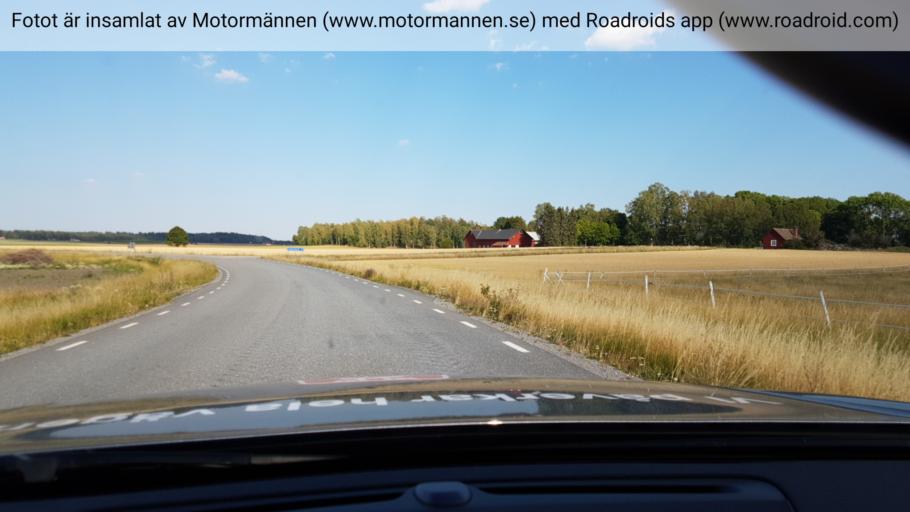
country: SE
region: Uppsala
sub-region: Enkopings Kommun
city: Enkoping
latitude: 59.7070
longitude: 17.0378
